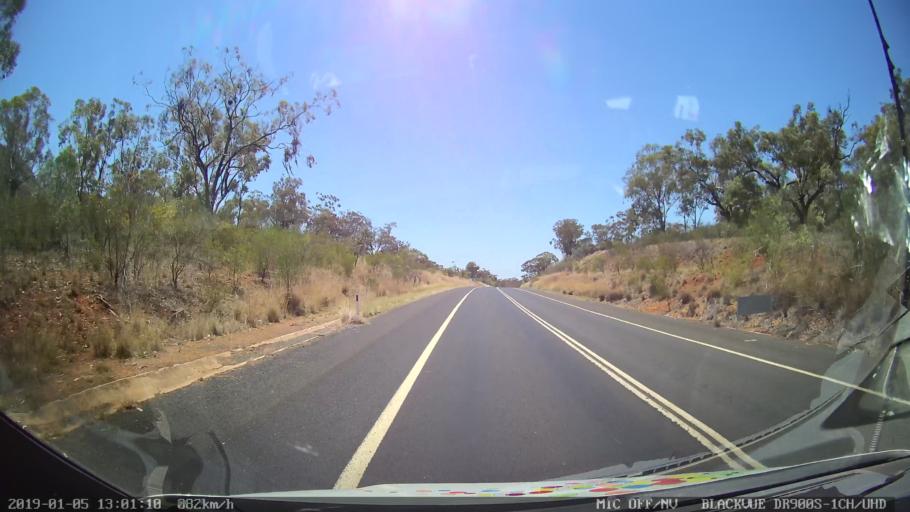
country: AU
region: New South Wales
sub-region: Narrabri
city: Boggabri
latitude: -31.1143
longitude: 149.7934
